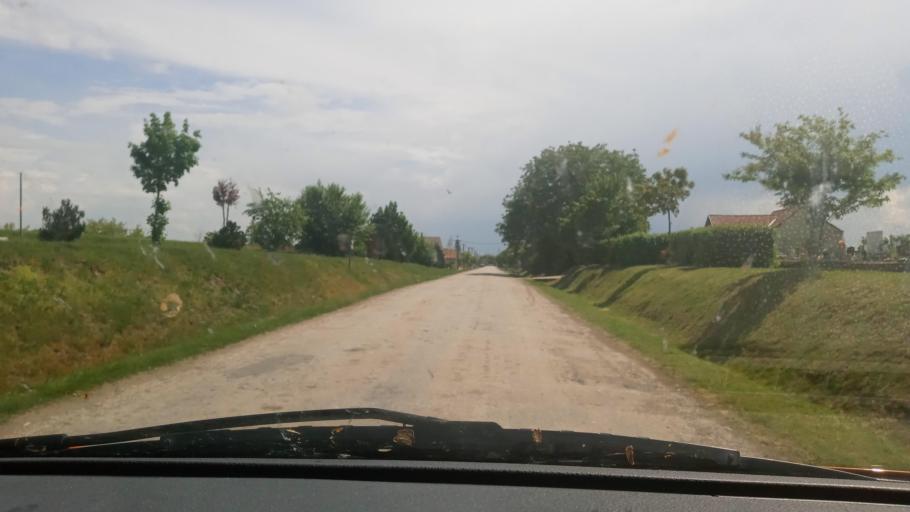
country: HU
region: Baranya
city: Siklos
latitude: 45.7957
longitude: 18.3501
